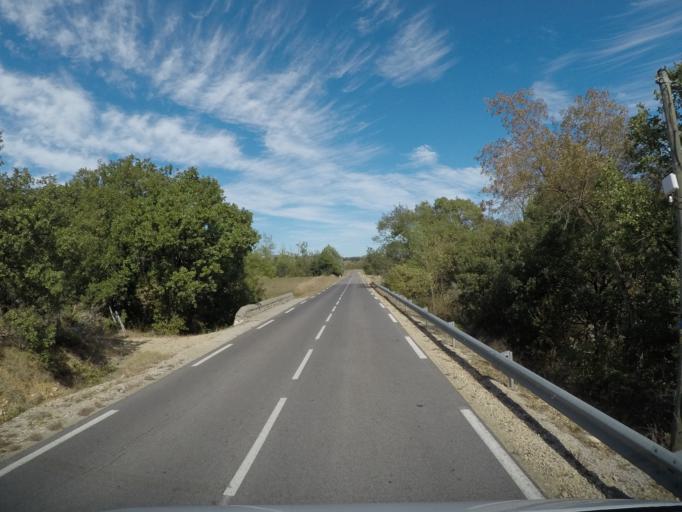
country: FR
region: Languedoc-Roussillon
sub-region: Departement de l'Herault
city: Saint-Bauzille-de-Putois
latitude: 43.9149
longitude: 3.7772
